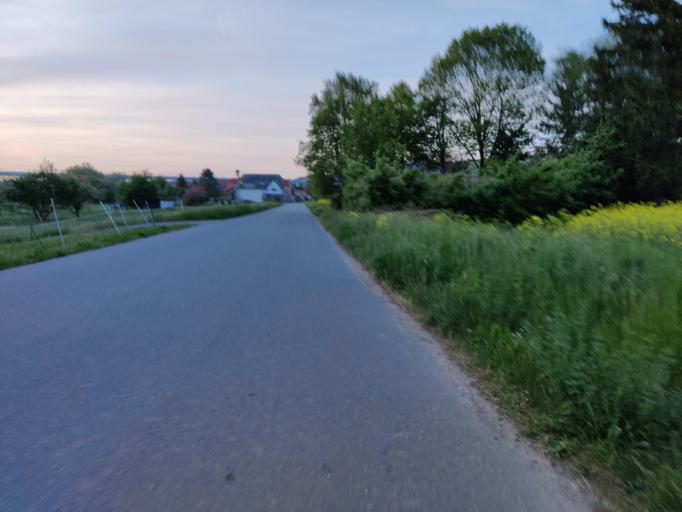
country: DE
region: Saxony-Anhalt
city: Karsdorf
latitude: 51.2757
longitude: 11.6520
